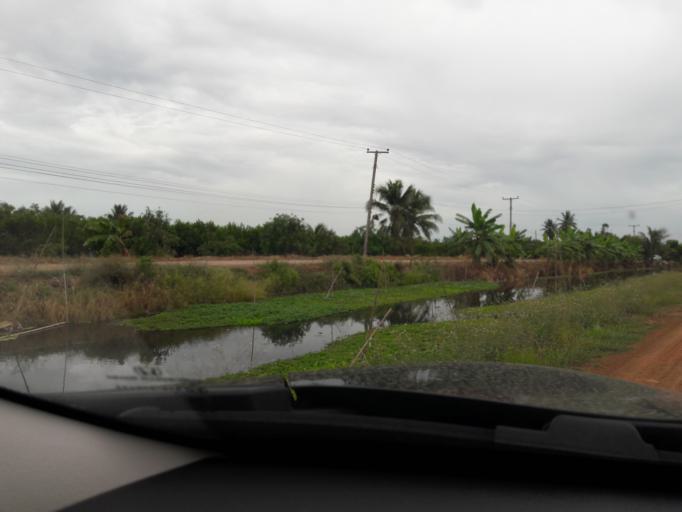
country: TH
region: Ratchaburi
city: Bang Phae
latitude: 13.6171
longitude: 99.9641
